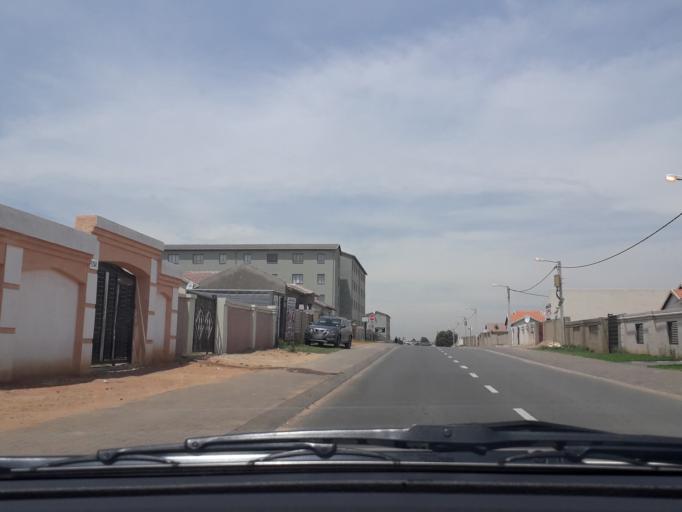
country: ZA
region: Gauteng
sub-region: City of Johannesburg Metropolitan Municipality
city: Roodepoort
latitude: -26.2036
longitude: 27.9122
